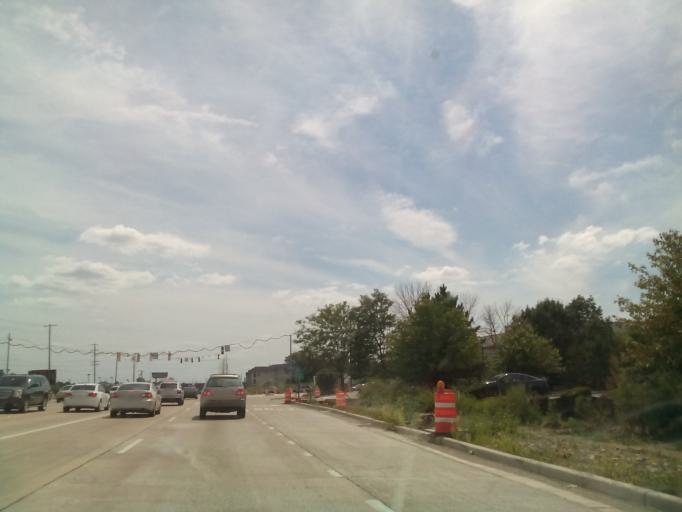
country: US
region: Illinois
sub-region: DuPage County
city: Warrenville
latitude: 41.7825
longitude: -88.2059
